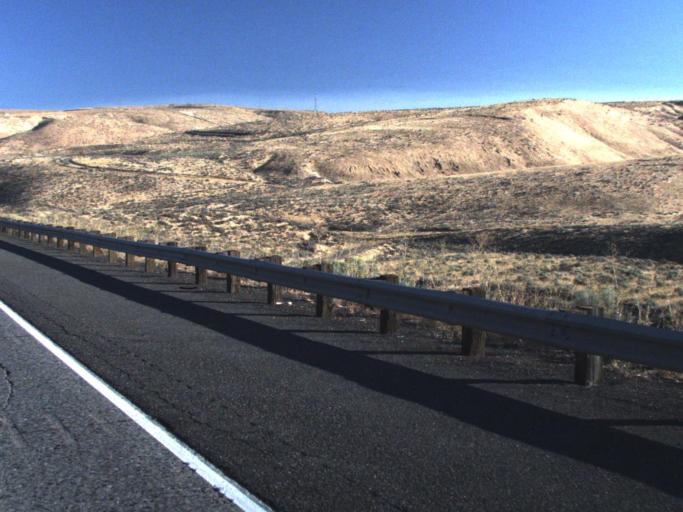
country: US
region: Washington
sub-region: Yakima County
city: Terrace Heights
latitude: 46.7386
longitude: -120.3860
